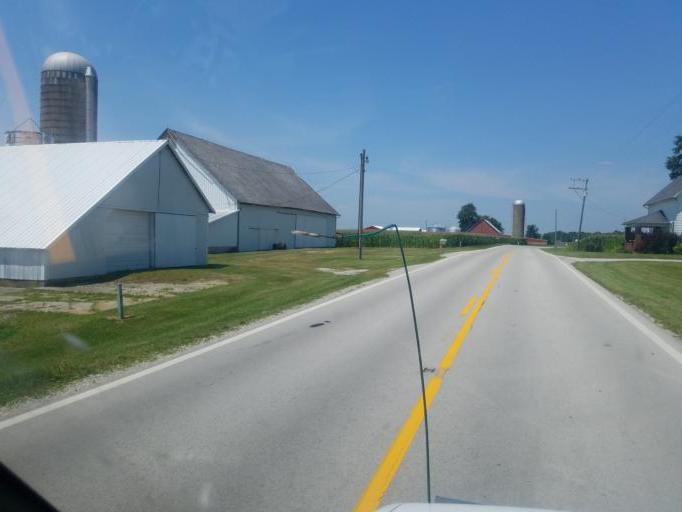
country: US
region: Ohio
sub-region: Shelby County
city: Fort Loramie
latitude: 40.3527
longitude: -84.4346
